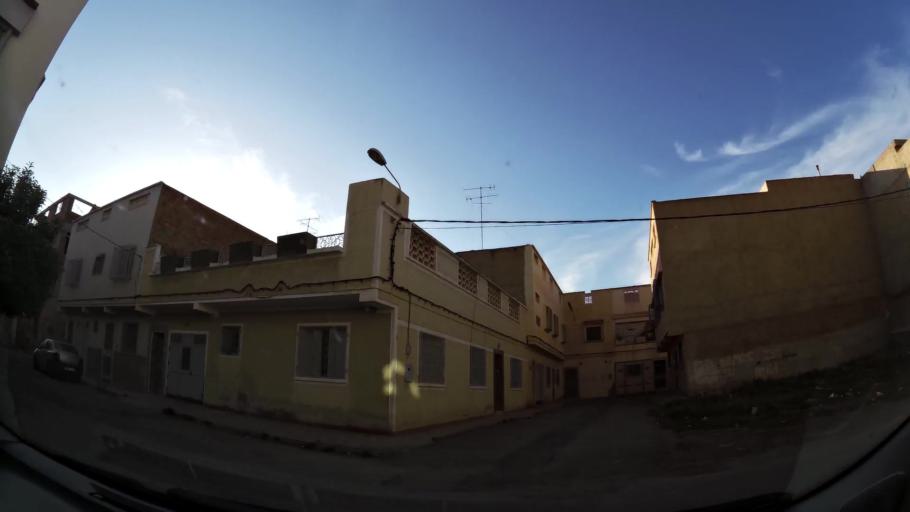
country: MA
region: Oriental
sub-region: Oujda-Angad
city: Oujda
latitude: 34.6968
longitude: -1.9040
